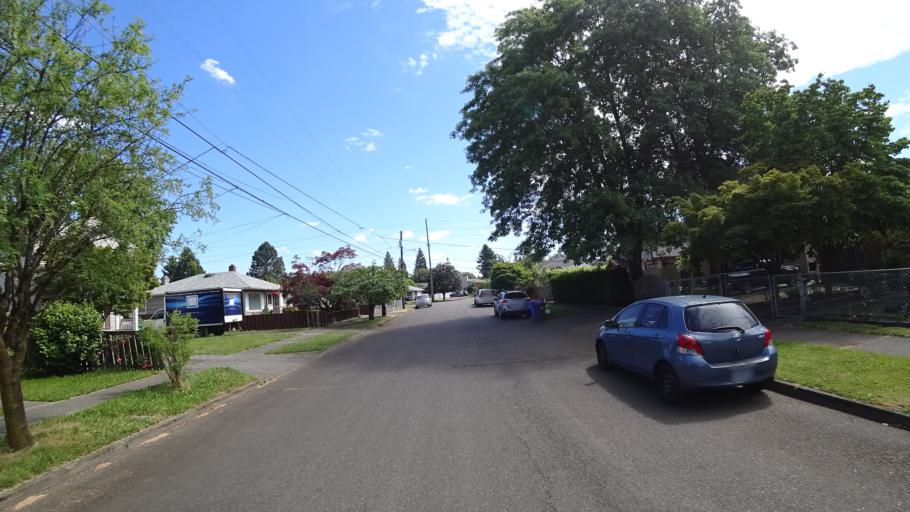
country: US
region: Oregon
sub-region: Multnomah County
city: Portland
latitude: 45.5873
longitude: -122.7264
